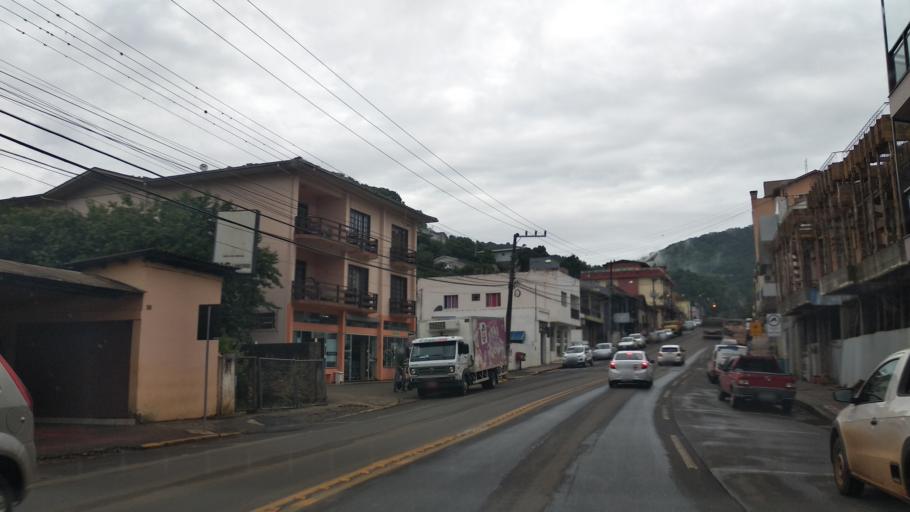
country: BR
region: Santa Catarina
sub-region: Videira
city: Videira
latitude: -27.1028
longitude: -51.2431
